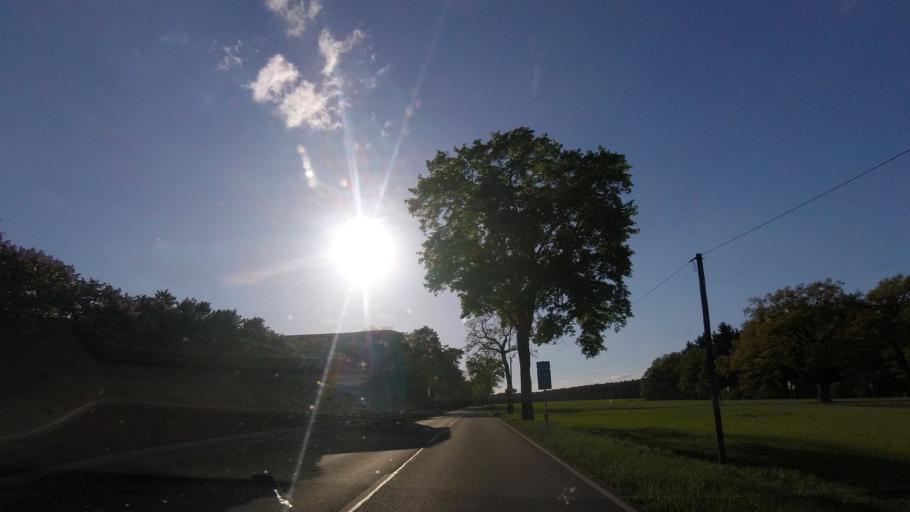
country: DE
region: Brandenburg
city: Kasel-Golzig
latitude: 51.9687
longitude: 13.6858
